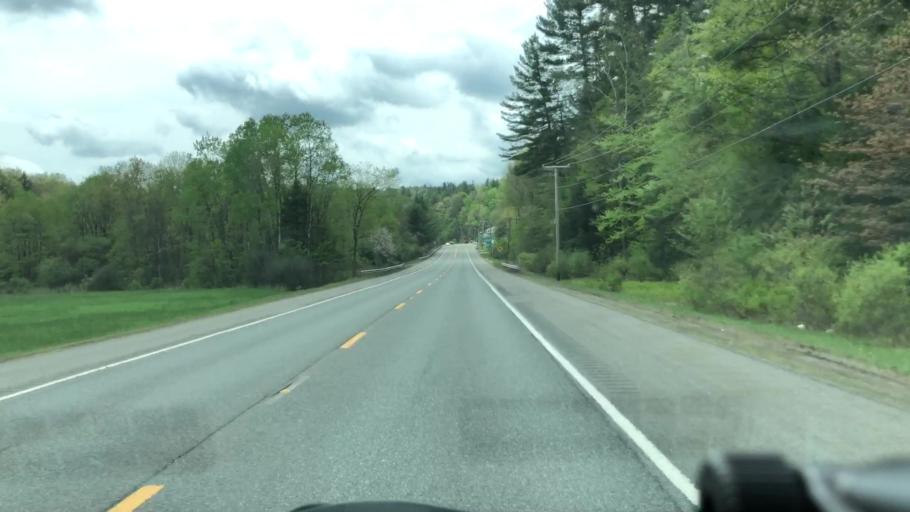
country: US
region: Massachusetts
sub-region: Hampshire County
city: Chesterfield
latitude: 42.4675
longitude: -72.9065
